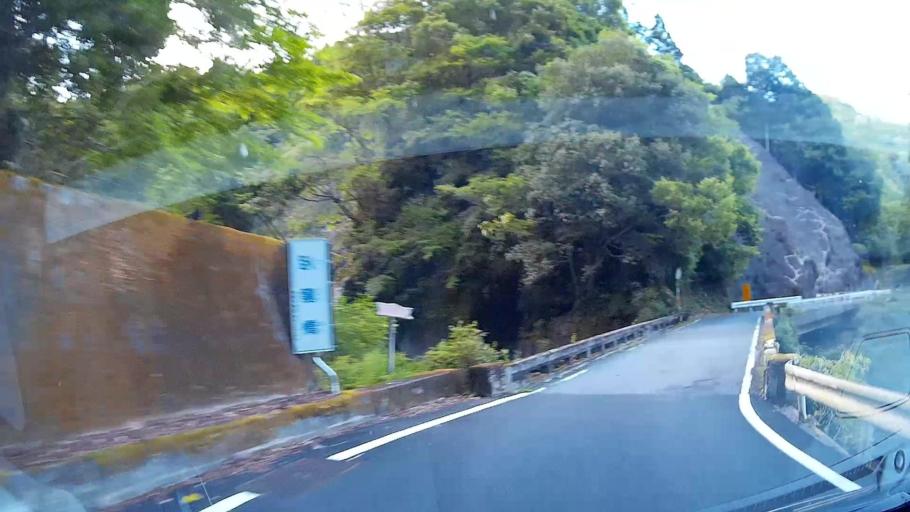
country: JP
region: Shizuoka
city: Shizuoka-shi
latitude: 35.1367
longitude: 138.2723
